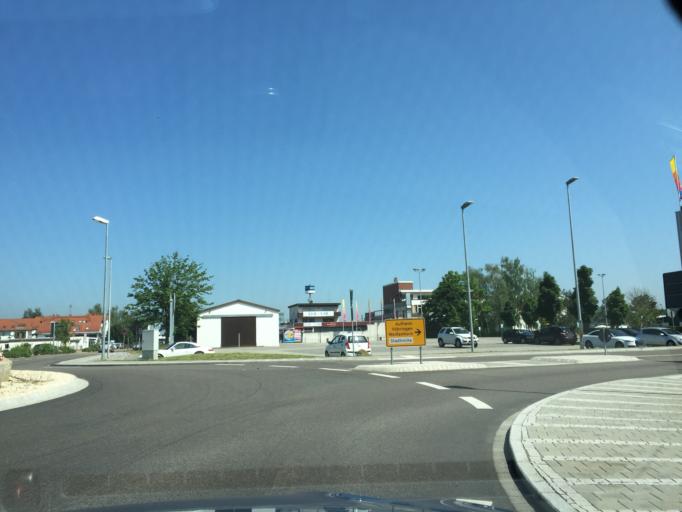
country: DE
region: Bavaria
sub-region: Swabia
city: Senden
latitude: 48.3289
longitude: 10.0350
